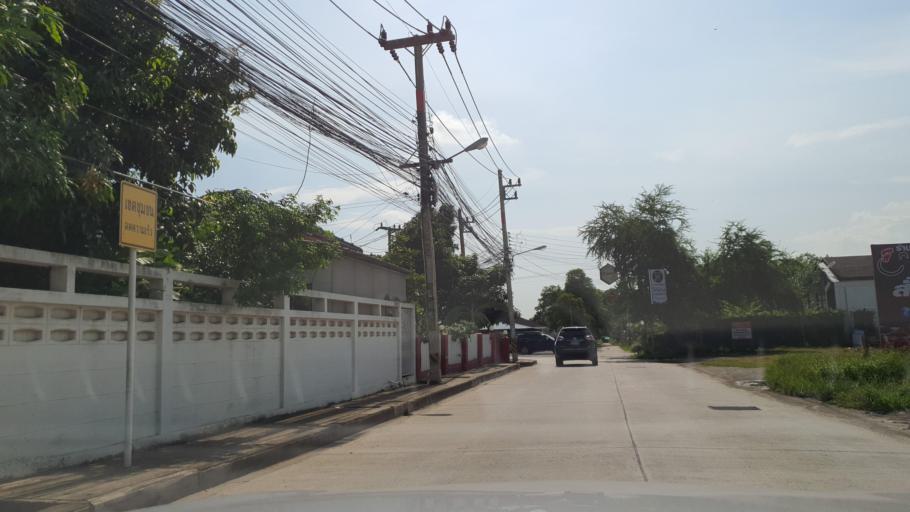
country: TH
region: Chachoengsao
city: Chachoengsao
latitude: 13.6811
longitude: 101.0651
